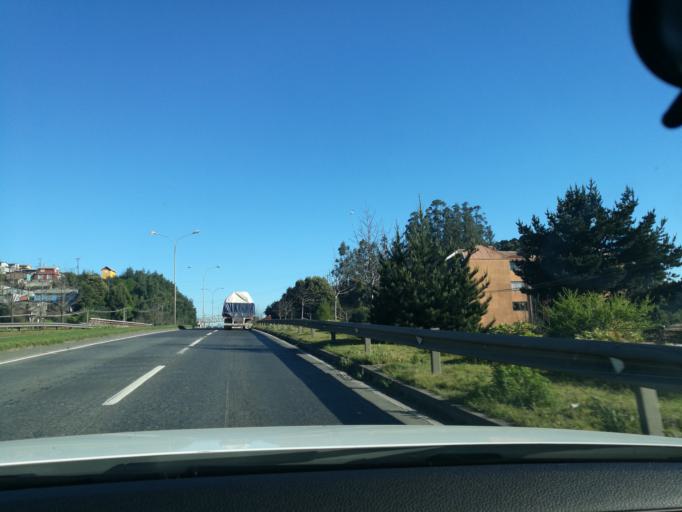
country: CL
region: Biobio
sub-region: Provincia de Concepcion
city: Concepcion
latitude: -36.8082
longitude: -73.0319
